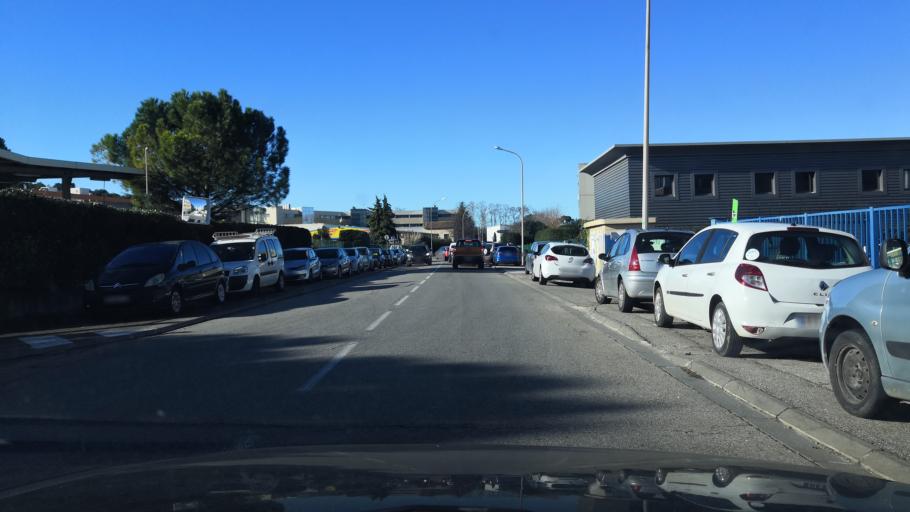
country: FR
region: Provence-Alpes-Cote d'Azur
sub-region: Departement des Bouches-du-Rhone
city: Aubagne
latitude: 43.2846
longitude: 5.5981
